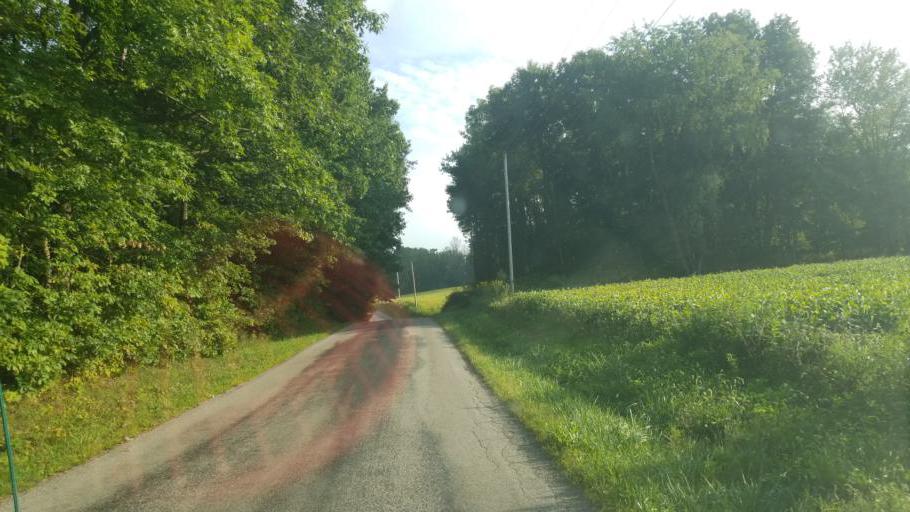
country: US
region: Ohio
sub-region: Wayne County
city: West Salem
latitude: 40.8977
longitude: -82.0238
